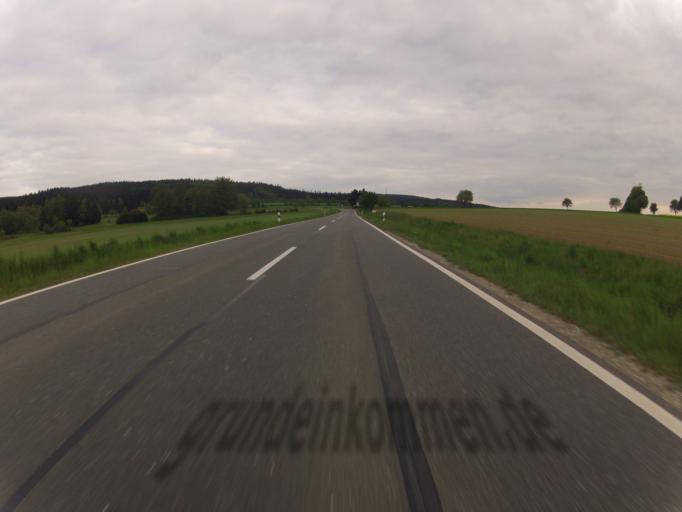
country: DE
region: Bavaria
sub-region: Upper Franconia
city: Sparneck
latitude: 50.1566
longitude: 11.8497
